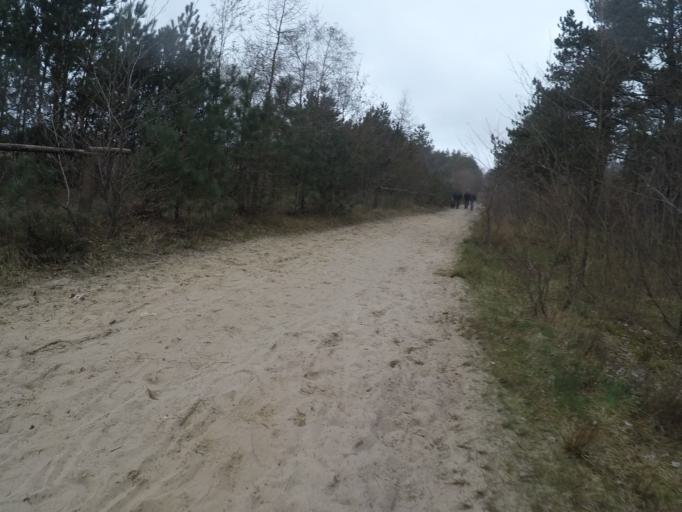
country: DE
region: Lower Saxony
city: Nordholz
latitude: 53.8281
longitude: 8.6447
